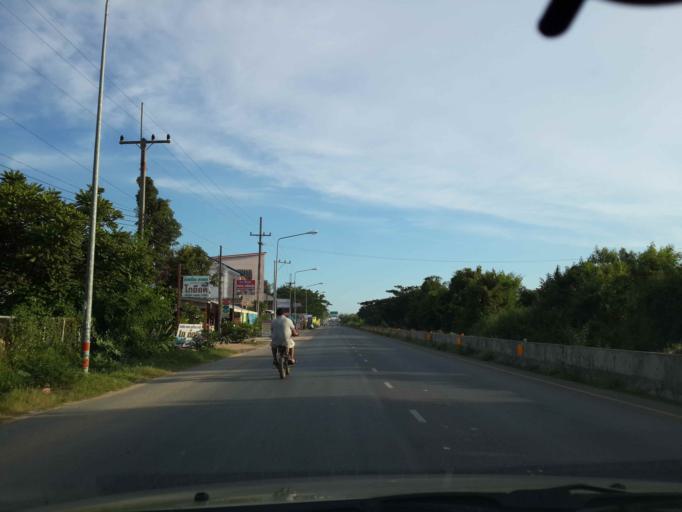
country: TH
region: Chon Buri
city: Phatthaya
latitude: 12.9548
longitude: 100.9169
